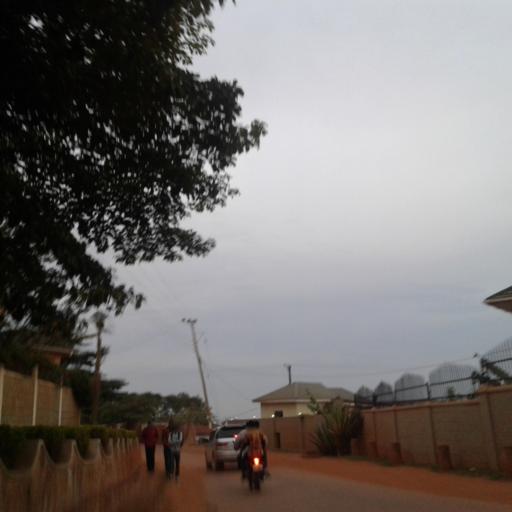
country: UG
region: Central Region
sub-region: Kampala District
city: Kampala
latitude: 0.2493
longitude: 32.6211
